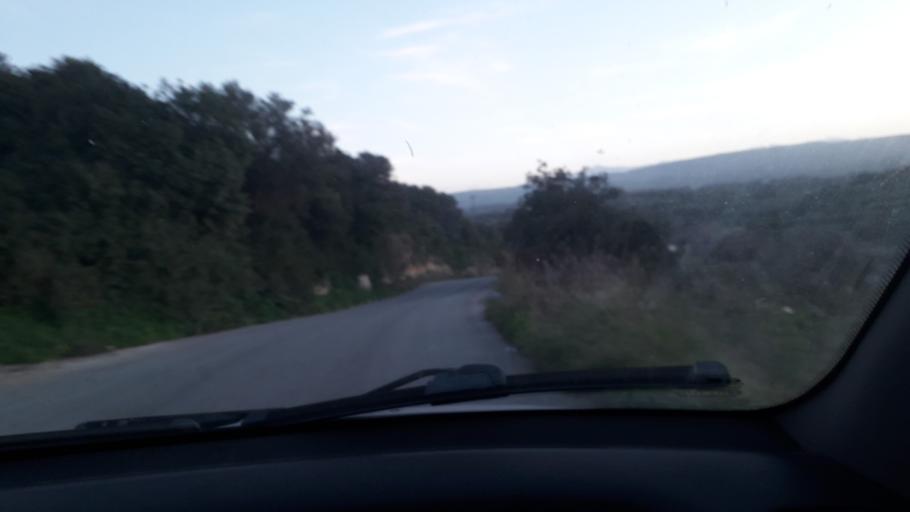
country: GR
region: Crete
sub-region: Nomos Rethymnis
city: Panormos
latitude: 35.3835
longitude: 24.6237
